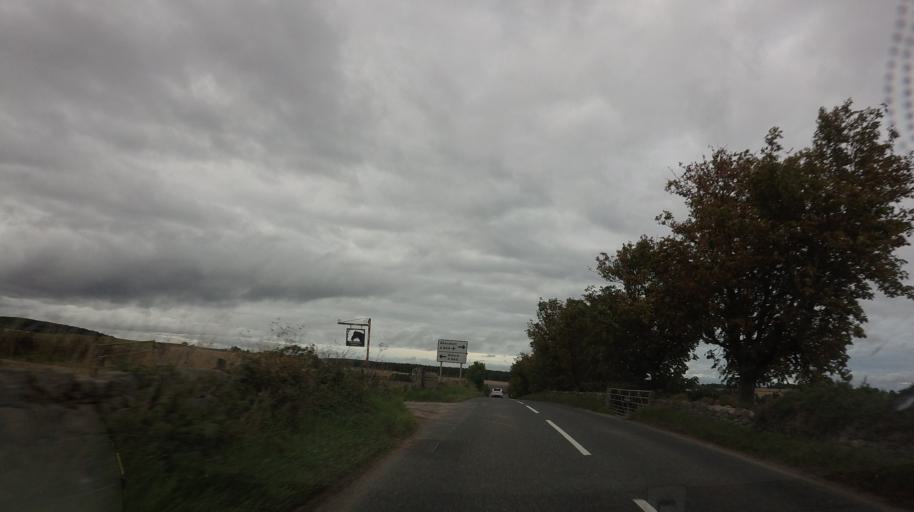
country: GB
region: Scotland
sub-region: Aberdeenshire
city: Kemnay
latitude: 57.1711
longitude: -2.4163
